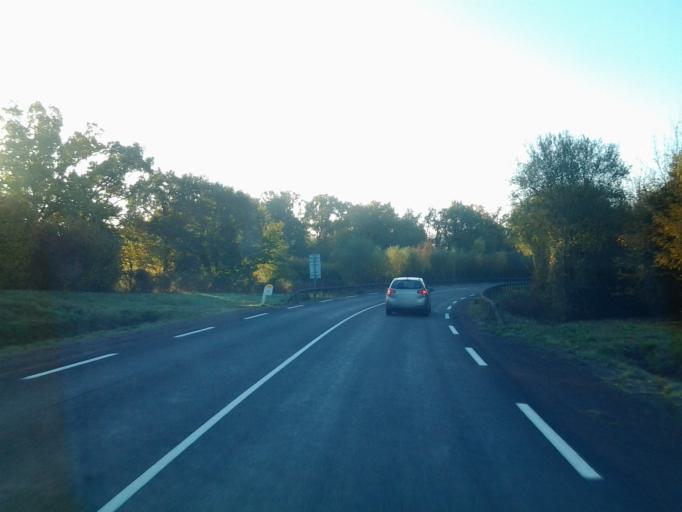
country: FR
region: Pays de la Loire
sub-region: Departement de la Vendee
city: La Ferriere
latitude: 46.6694
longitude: -1.3609
